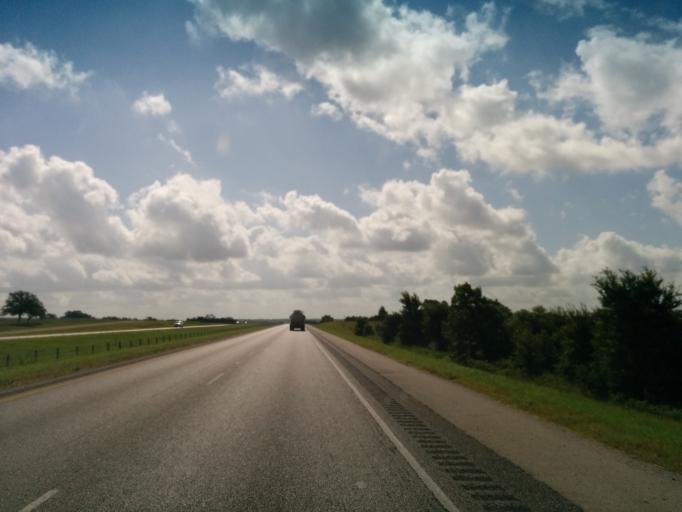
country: US
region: Texas
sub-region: Fayette County
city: Schulenburg
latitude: 29.6895
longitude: -96.9648
